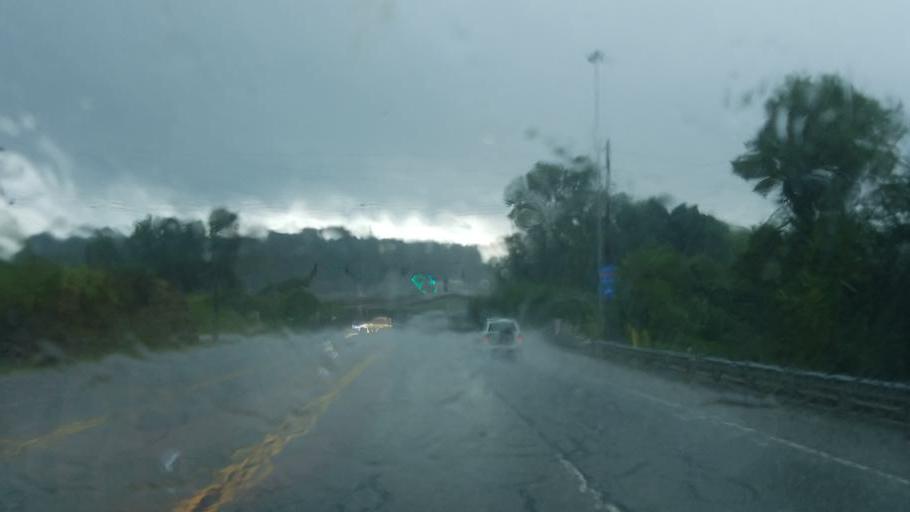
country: US
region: Kentucky
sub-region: Rowan County
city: Morehead
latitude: 38.1937
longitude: -83.4799
